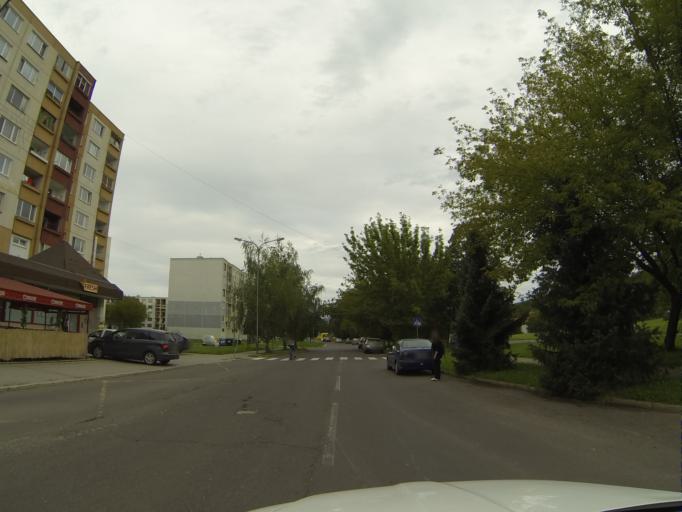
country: SK
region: Nitriansky
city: Prievidza
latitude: 48.7841
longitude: 18.6334
